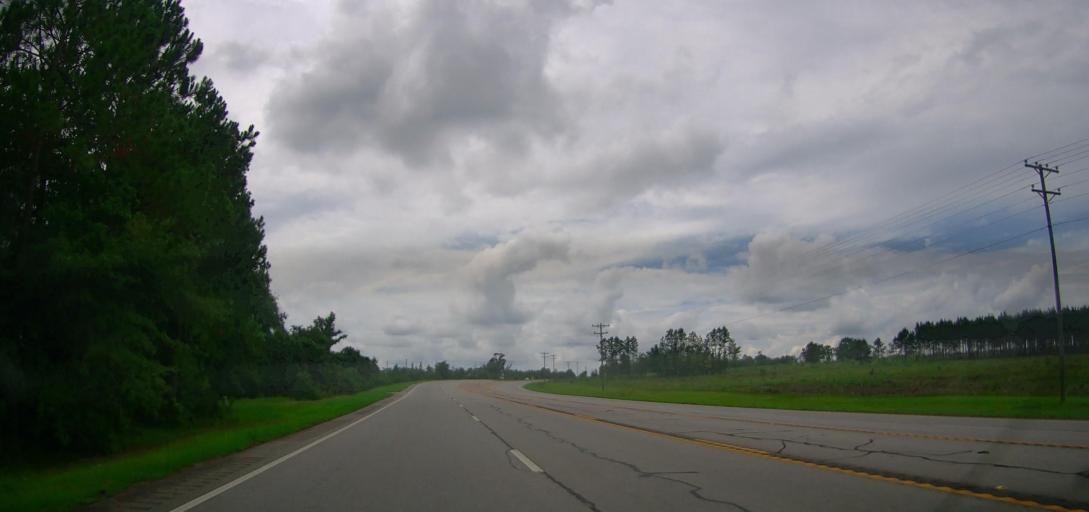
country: US
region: Georgia
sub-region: Telfair County
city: Lumber City
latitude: 31.9428
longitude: -82.7013
